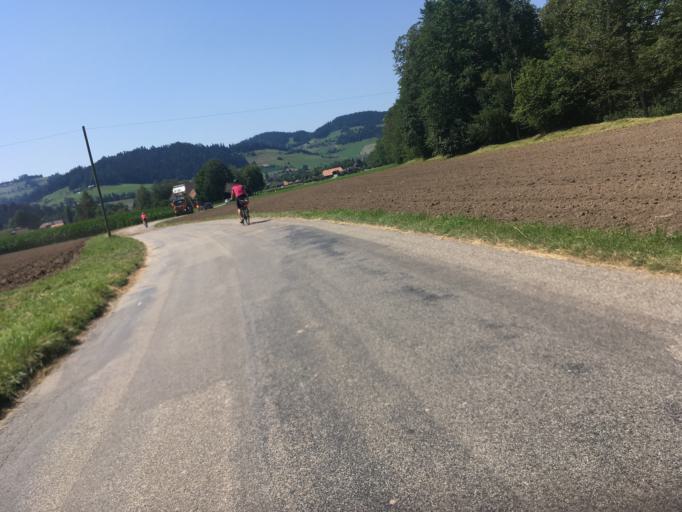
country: CH
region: Bern
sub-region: Emmental District
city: Langnau
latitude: 46.9448
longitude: 7.7632
